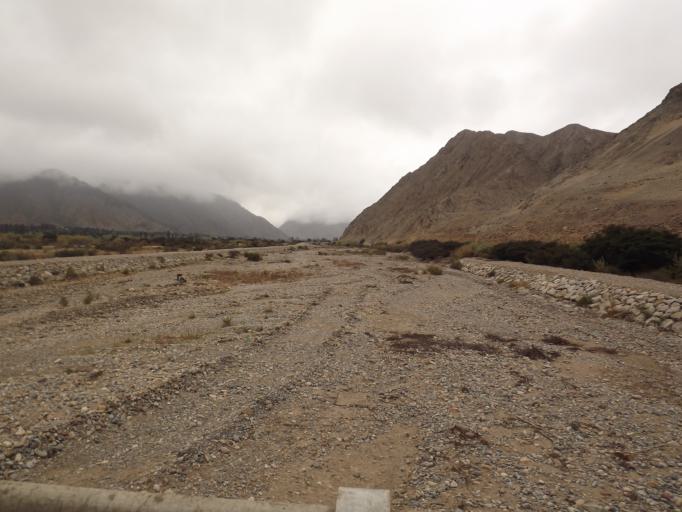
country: PE
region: Lima
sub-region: Huaura
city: Vegueta
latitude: -10.8934
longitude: -77.5110
